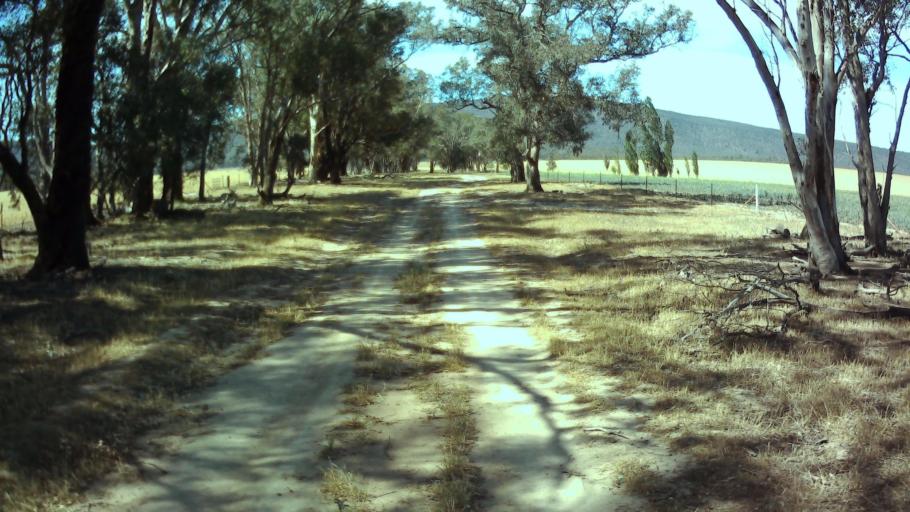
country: AU
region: New South Wales
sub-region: Weddin
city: Grenfell
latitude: -33.9439
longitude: 148.0470
